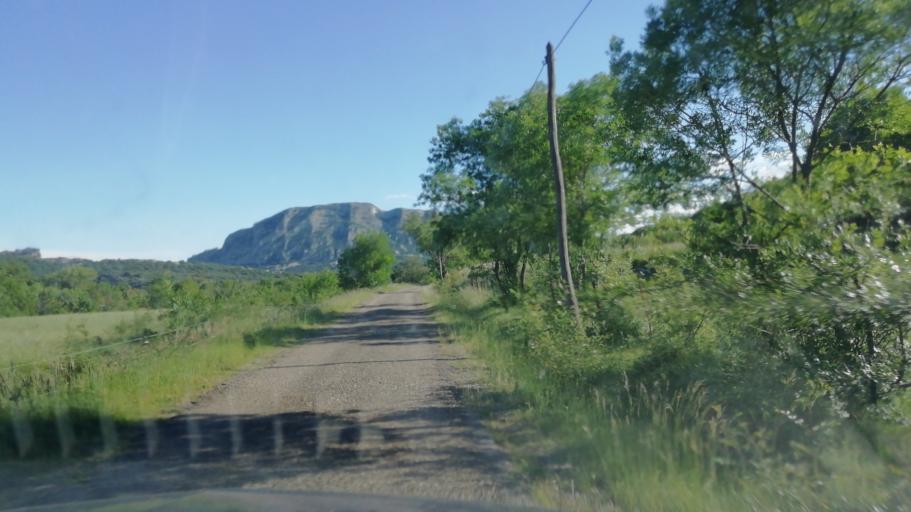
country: FR
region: Languedoc-Roussillon
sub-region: Departement de l'Herault
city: Saint-Mathieu-de-Treviers
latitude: 43.8069
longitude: 3.8098
